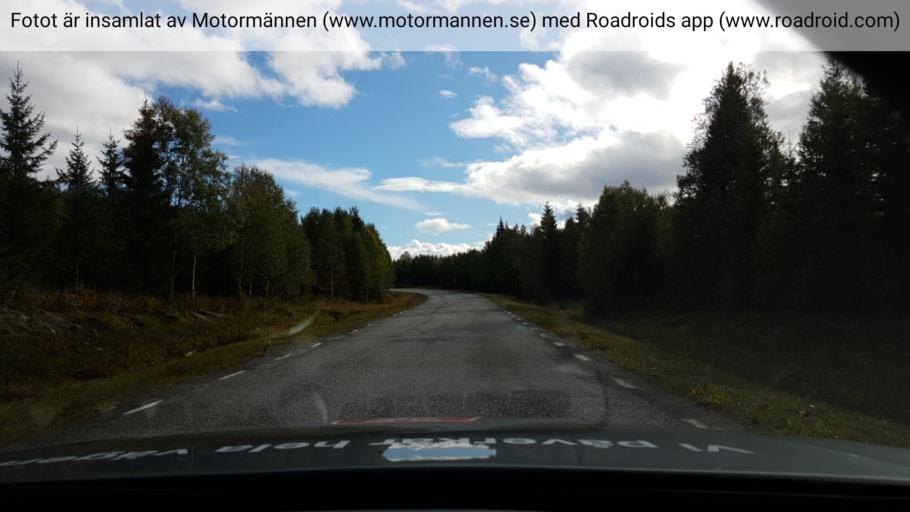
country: SE
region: Jaemtland
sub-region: Are Kommun
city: Are
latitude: 63.7360
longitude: 13.0550
